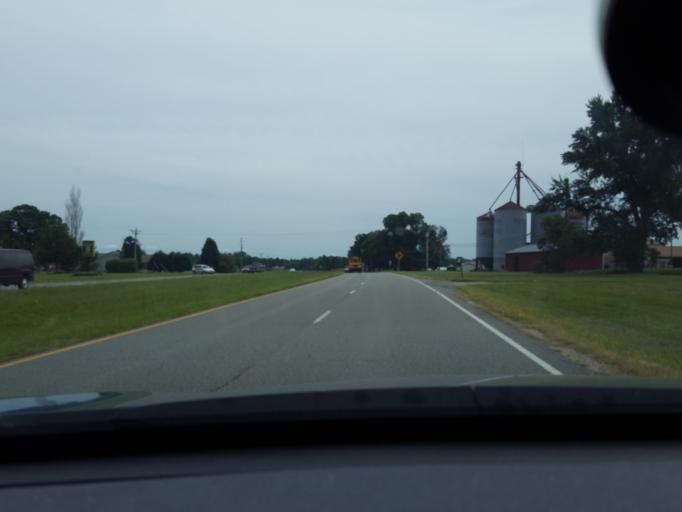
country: US
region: Virginia
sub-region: Caroline County
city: Bowling Green
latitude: 38.0201
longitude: -77.3388
